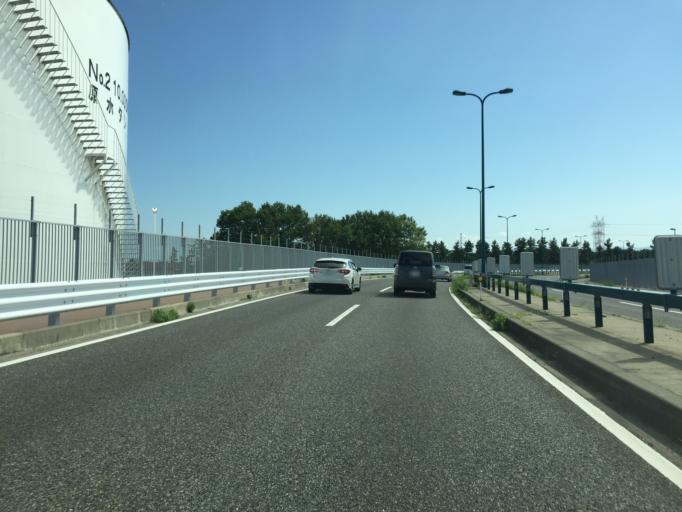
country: JP
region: Niigata
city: Niigata-shi
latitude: 37.9469
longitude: 139.0840
